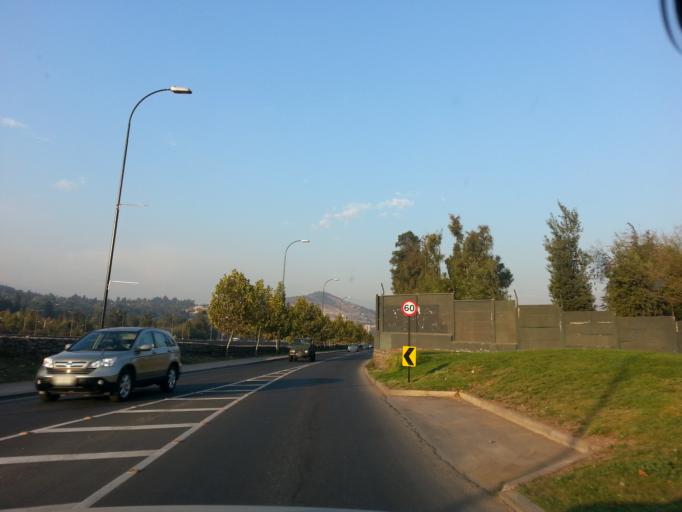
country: CL
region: Santiago Metropolitan
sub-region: Provincia de Santiago
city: Villa Presidente Frei, Nunoa, Santiago, Chile
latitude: -33.3783
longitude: -70.5677
